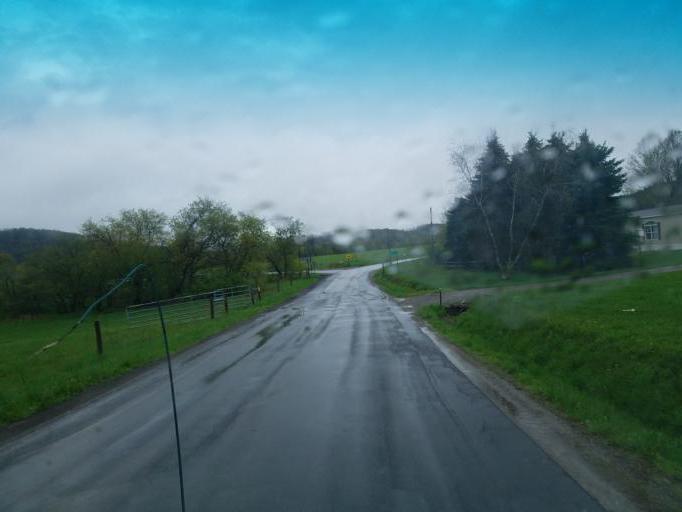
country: US
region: Pennsylvania
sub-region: Tioga County
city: Westfield
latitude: 41.9696
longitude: -77.6595
